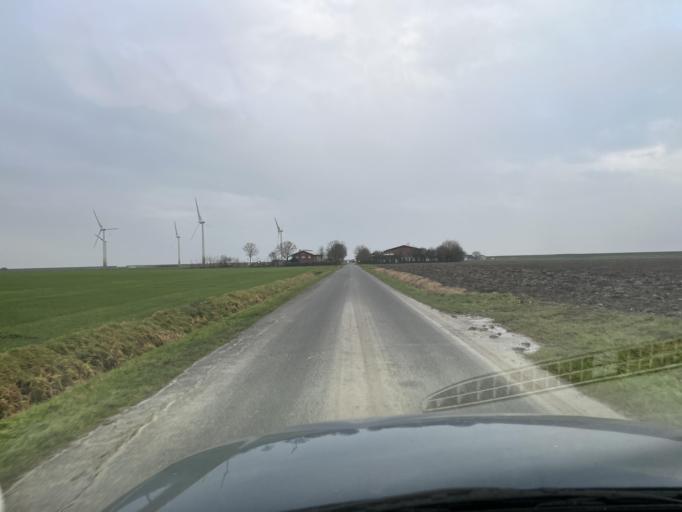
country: DE
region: Schleswig-Holstein
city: Hillgroven
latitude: 54.2196
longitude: 8.8702
